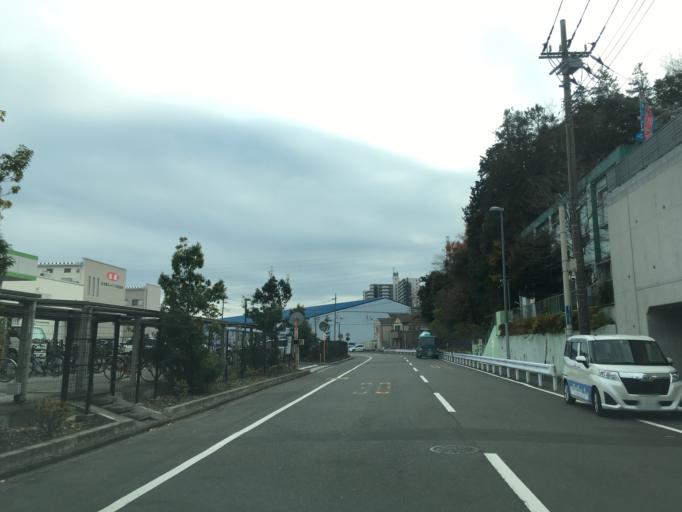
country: JP
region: Kanagawa
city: Minami-rinkan
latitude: 35.4983
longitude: 139.4630
